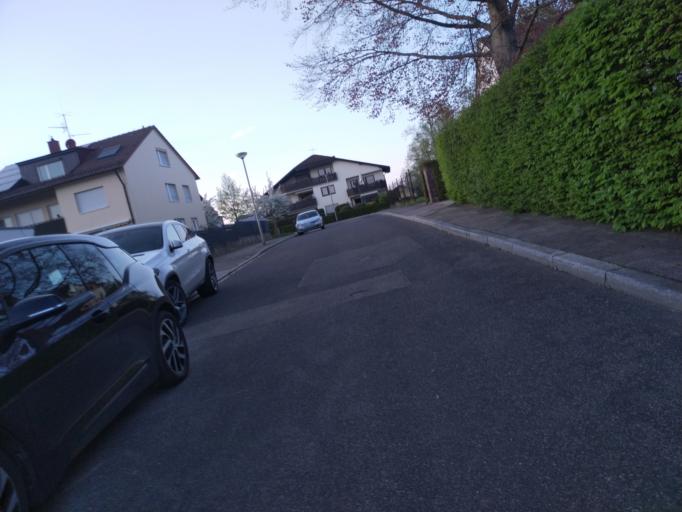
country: DE
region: Baden-Wuerttemberg
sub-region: Karlsruhe Region
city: Pforzheim
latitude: 48.8824
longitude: 8.6824
